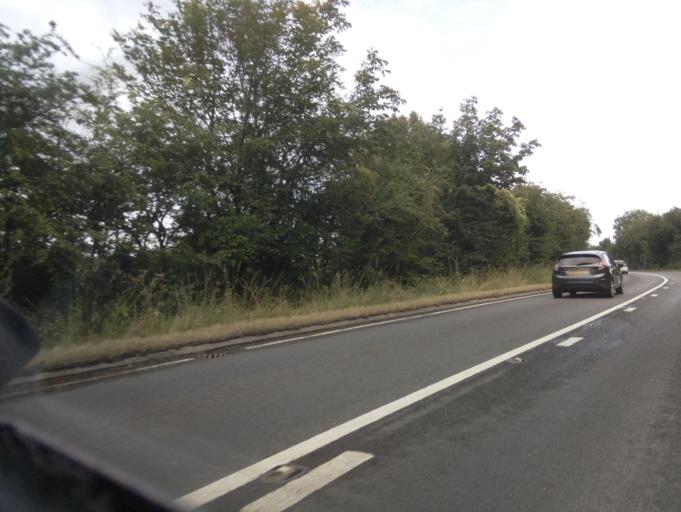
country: GB
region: England
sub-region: Warwickshire
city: Southam
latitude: 52.2635
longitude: -1.3842
